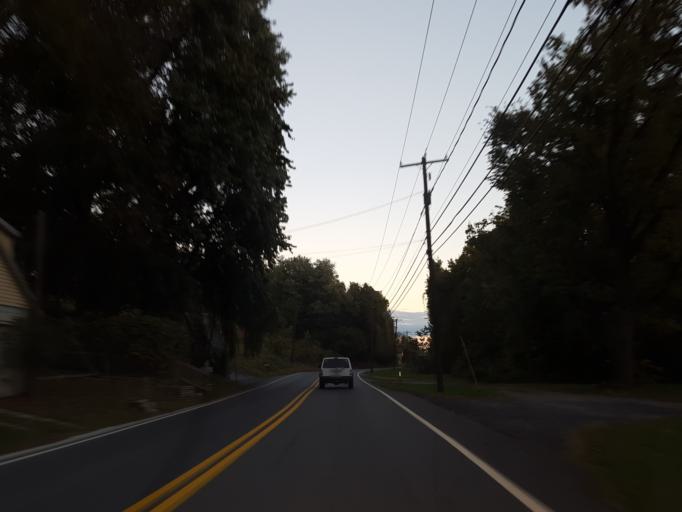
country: US
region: Pennsylvania
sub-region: Lancaster County
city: Columbia
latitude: 40.0092
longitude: -76.4810
